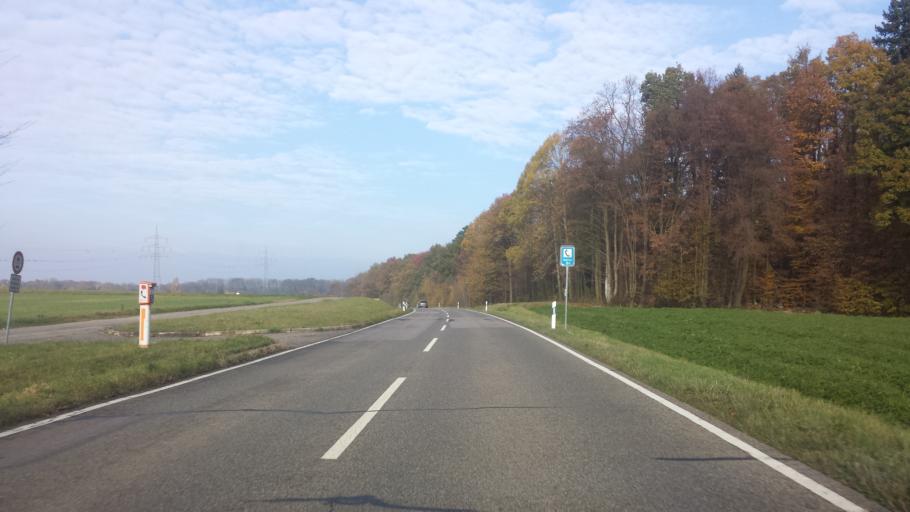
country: DE
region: Baden-Wuerttemberg
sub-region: Karlsruhe Region
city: Huffenhardt
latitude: 49.3156
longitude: 9.0752
